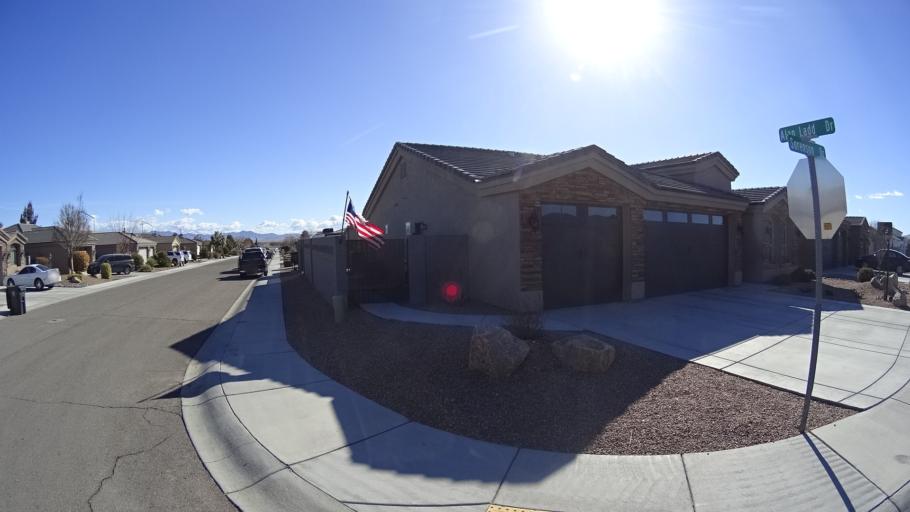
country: US
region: Arizona
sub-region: Mohave County
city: New Kingman-Butler
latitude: 35.2389
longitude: -114.0322
